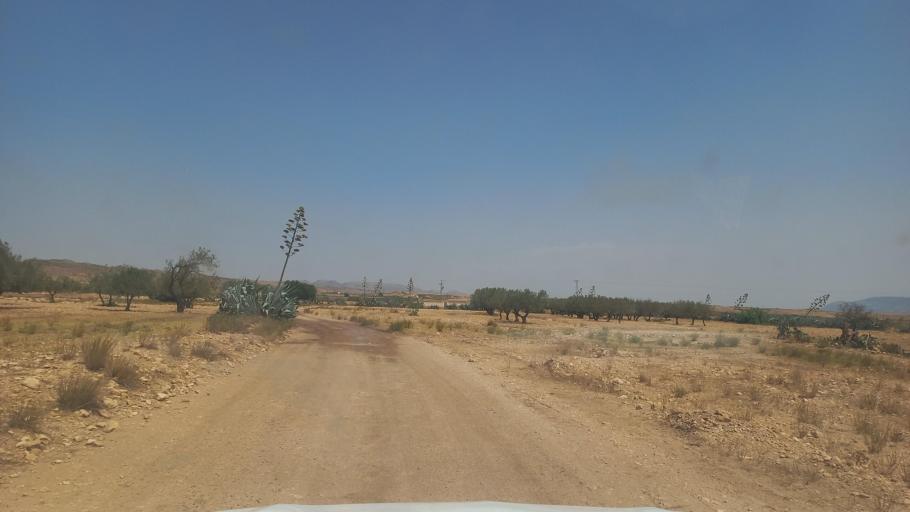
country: TN
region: Al Qasrayn
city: Kasserine
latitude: 35.2865
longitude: 8.9506
